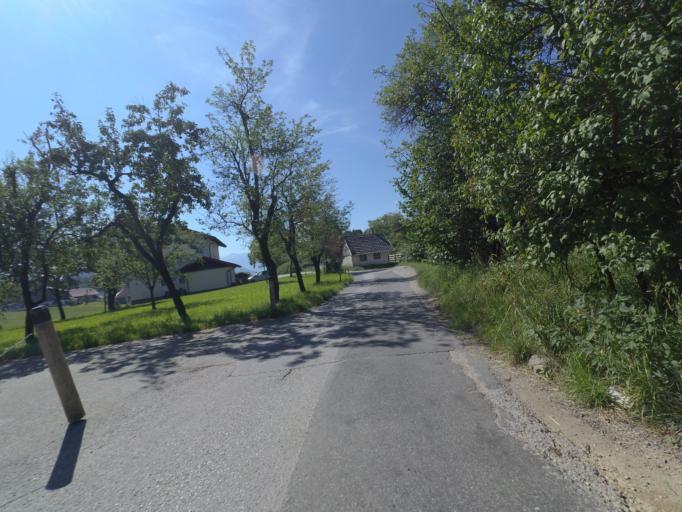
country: AT
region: Salzburg
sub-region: Politischer Bezirk Hallein
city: Adnet
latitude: 47.6721
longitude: 13.1407
